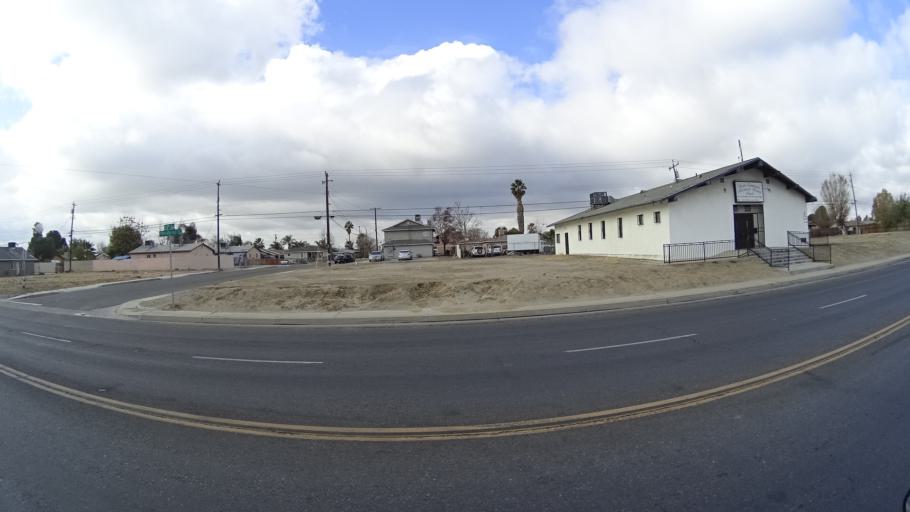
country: US
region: California
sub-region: Kern County
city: Bakersfield
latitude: 35.3597
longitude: -118.9852
